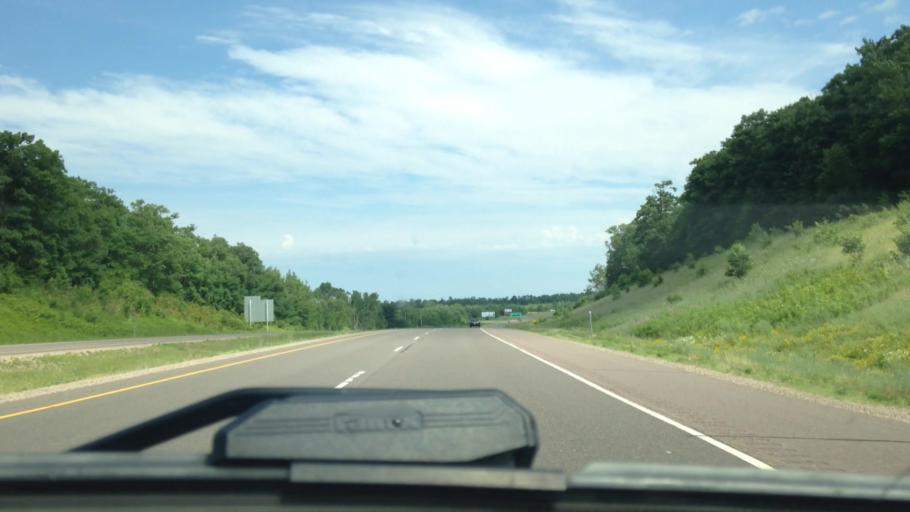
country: US
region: Wisconsin
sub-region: Washburn County
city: Spooner
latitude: 45.8352
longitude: -91.8599
